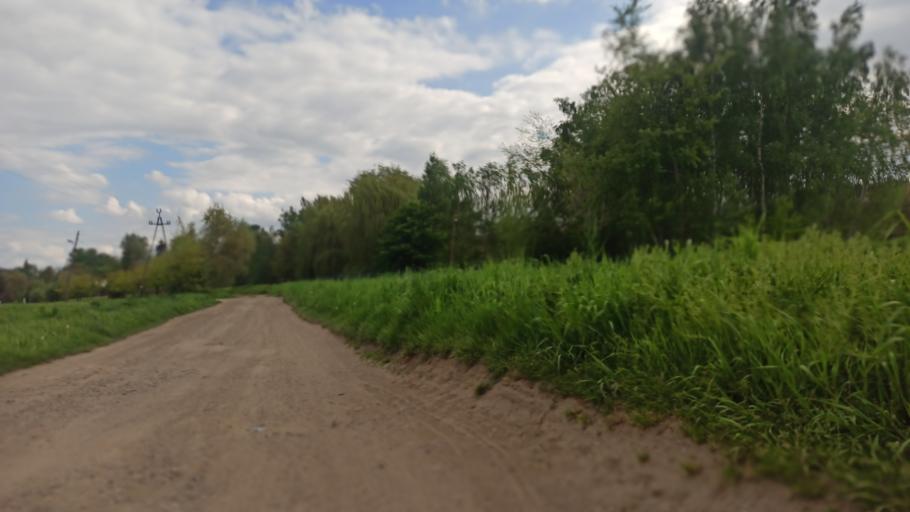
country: PL
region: Subcarpathian Voivodeship
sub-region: Powiat jaroslawski
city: Radymno
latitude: 49.9543
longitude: 22.8225
